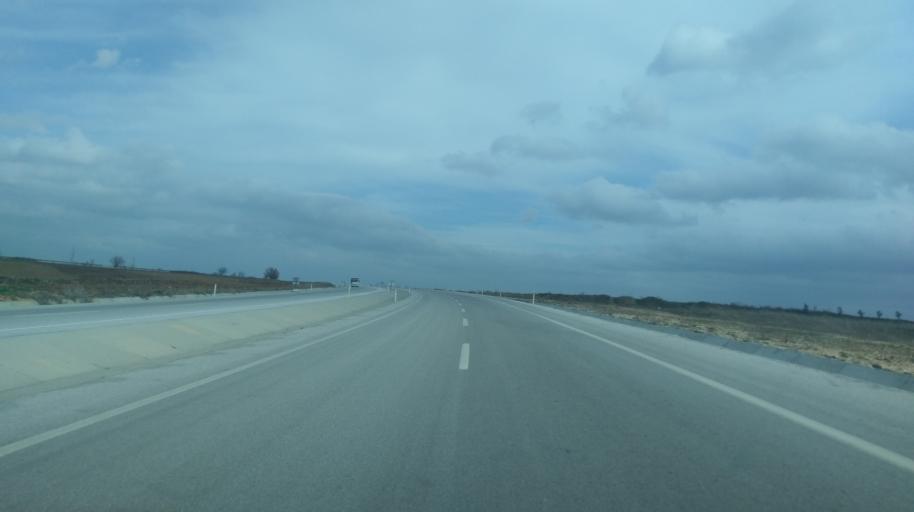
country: TR
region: Kirklareli
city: Inece
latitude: 41.6803
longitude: 27.1031
